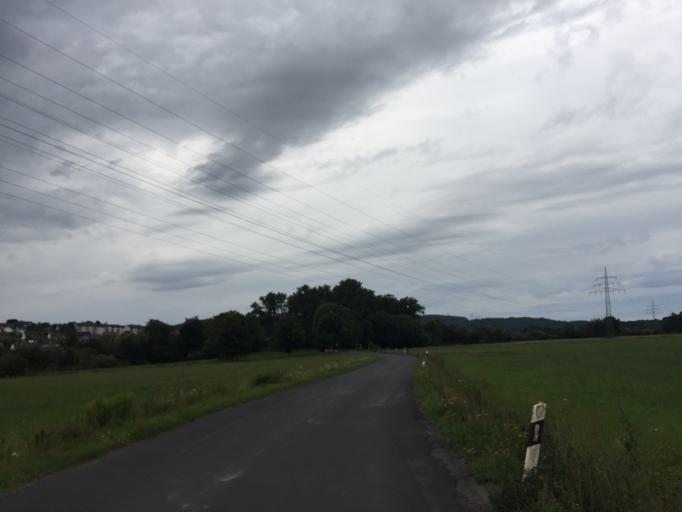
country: DE
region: Hesse
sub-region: Regierungsbezirk Kassel
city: Bad Hersfeld
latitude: 50.8939
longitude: 9.7460
